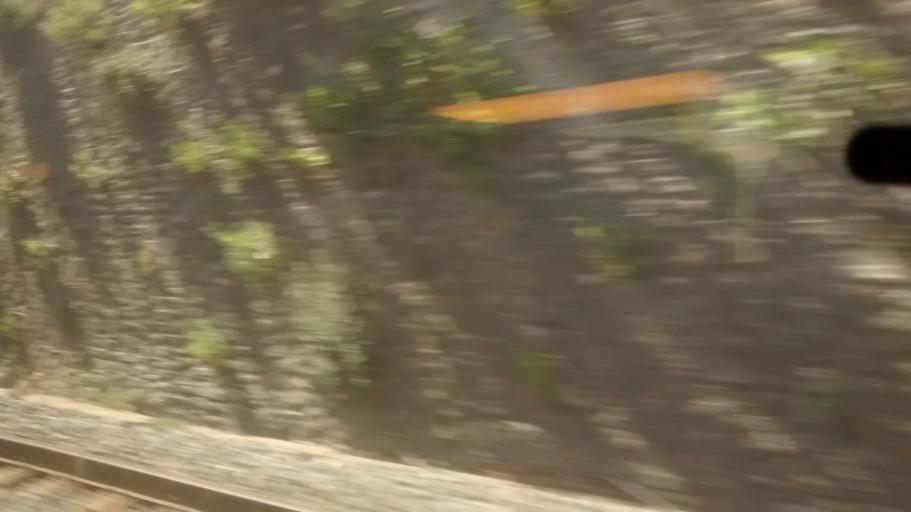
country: FR
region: Languedoc-Roussillon
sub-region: Departement du Gard
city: Milhaud
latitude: 43.7901
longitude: 4.3055
